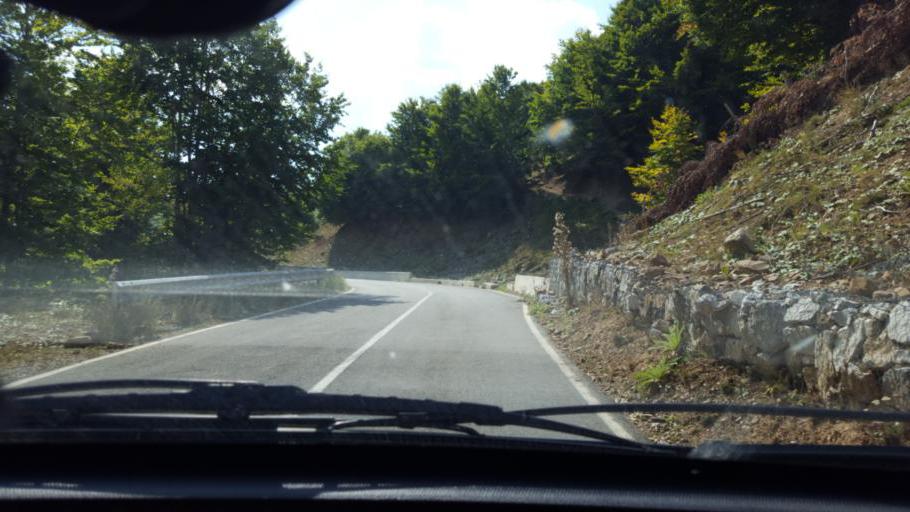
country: AL
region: Kukes
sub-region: Rrethi i Tropojes
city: Valbone
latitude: 42.5463
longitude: 19.7207
